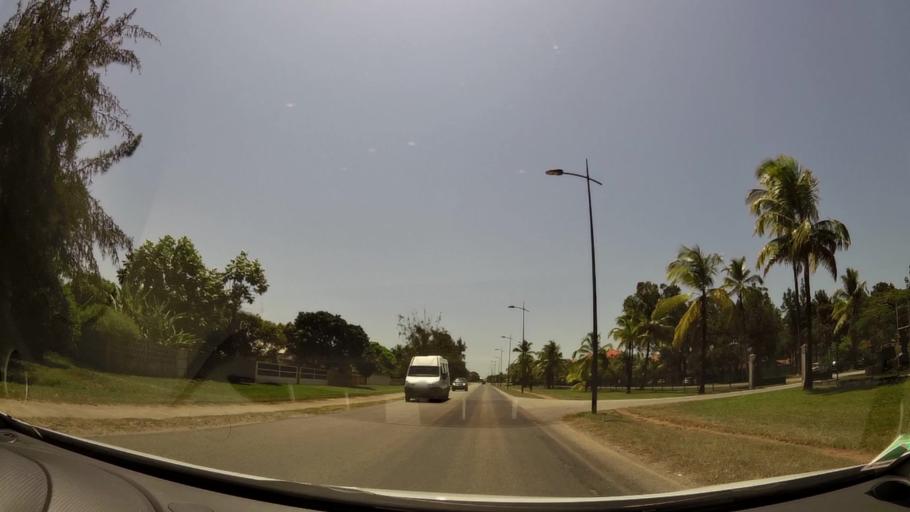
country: GF
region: Guyane
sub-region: Guyane
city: Kourou
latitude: 5.1705
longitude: -52.6481
